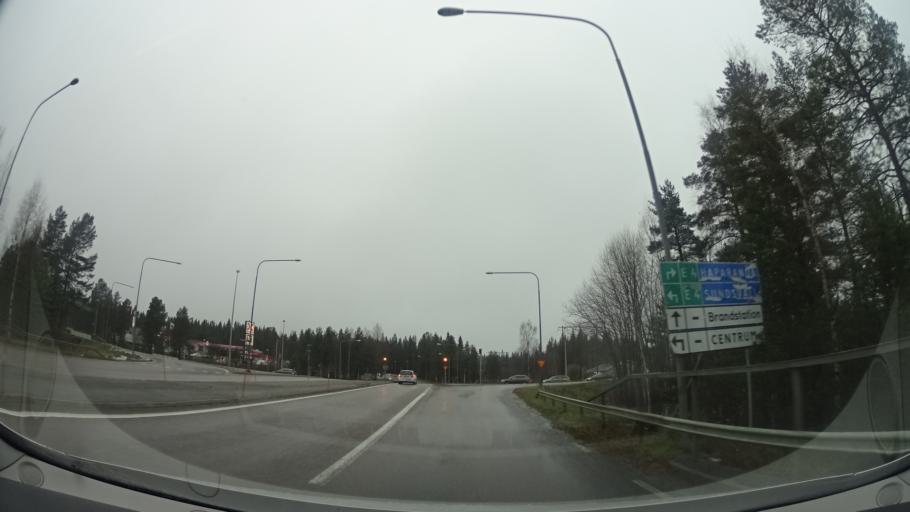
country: SE
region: Vaesterbotten
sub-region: Skelleftea Kommun
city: Skelleftea
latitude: 64.7616
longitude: 21.0051
